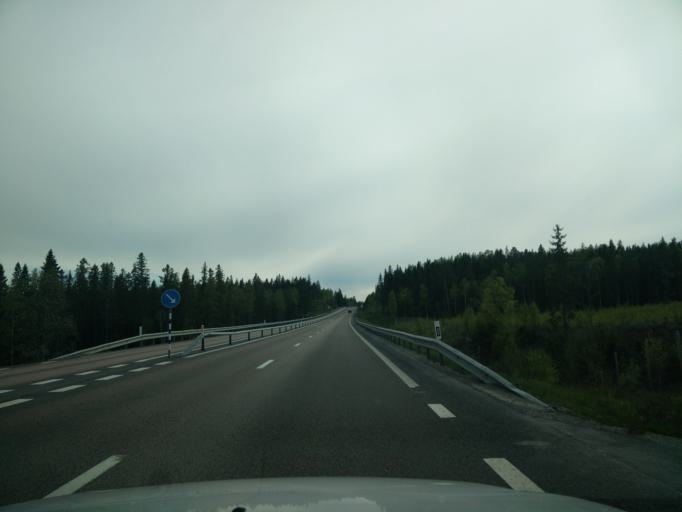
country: SE
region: Vaesternorrland
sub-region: OErnskoeldsviks Kommun
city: Bjasta
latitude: 63.1906
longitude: 18.4656
